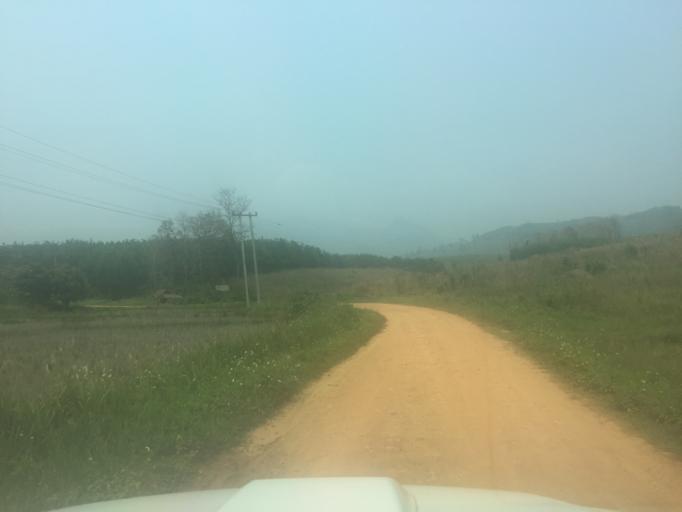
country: TH
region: Phayao
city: Phu Sang
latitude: 19.7723
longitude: 100.5374
